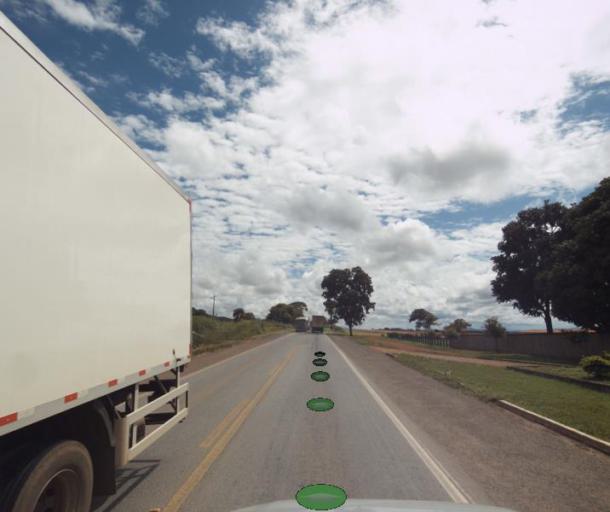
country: BR
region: Goias
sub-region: Uruacu
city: Uruacu
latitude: -14.4031
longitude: -49.1575
